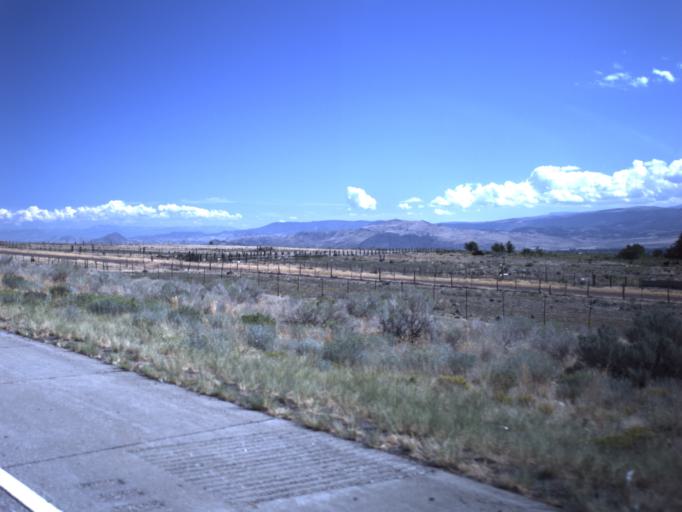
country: US
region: Utah
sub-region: Sevier County
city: Monroe
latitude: 38.7014
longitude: -112.1430
